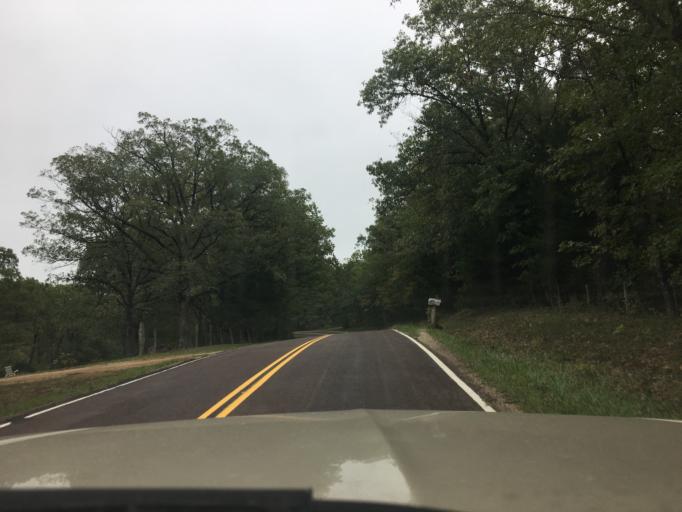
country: US
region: Missouri
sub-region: Crawford County
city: Cuba
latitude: 38.1985
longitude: -91.4516
